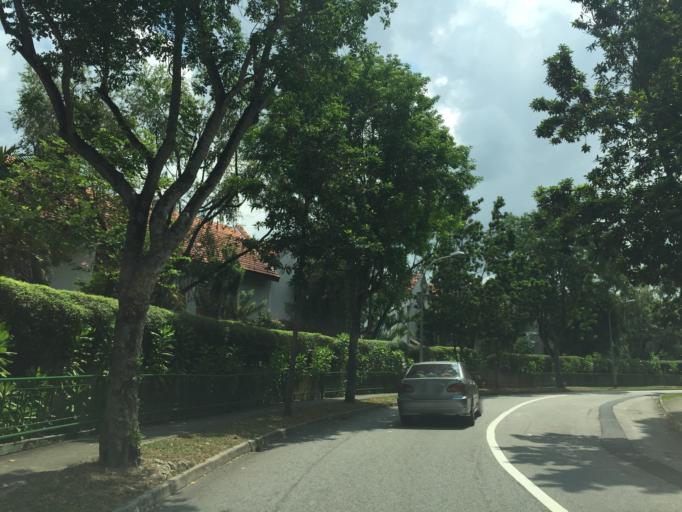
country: SG
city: Singapore
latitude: 1.3228
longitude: 103.8390
